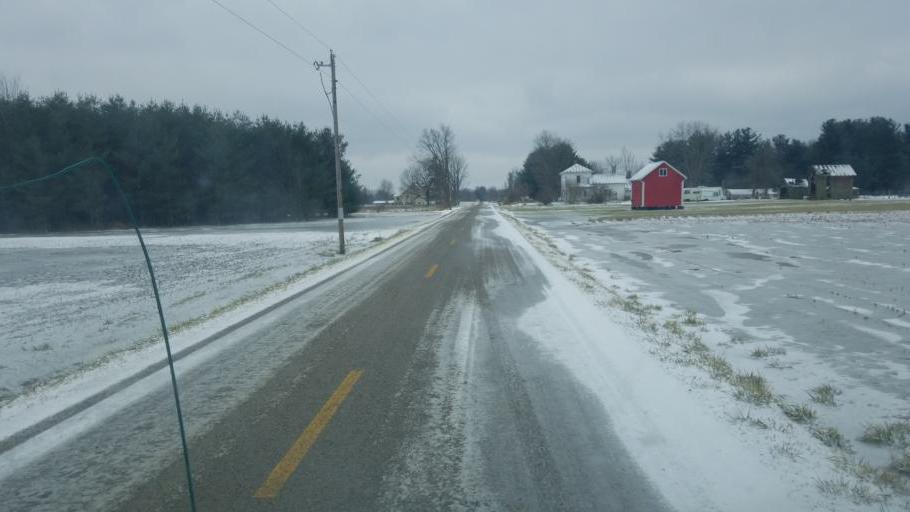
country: US
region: Ohio
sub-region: Knox County
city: Centerburg
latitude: 40.2966
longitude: -82.7732
